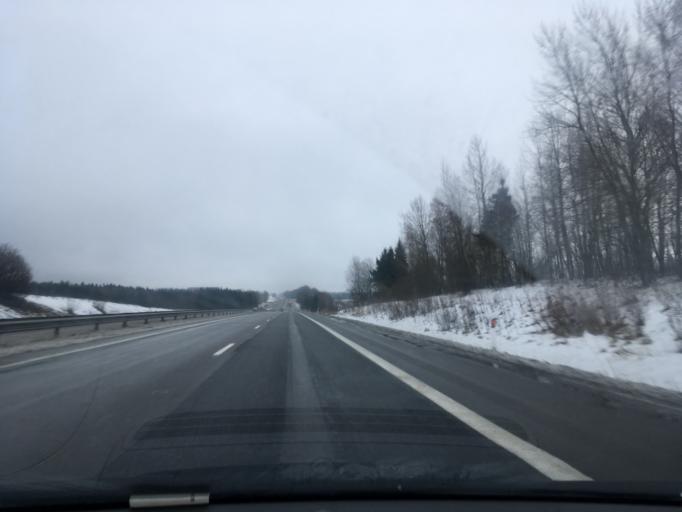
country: LT
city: Kaisiadorys
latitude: 54.8352
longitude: 24.3652
